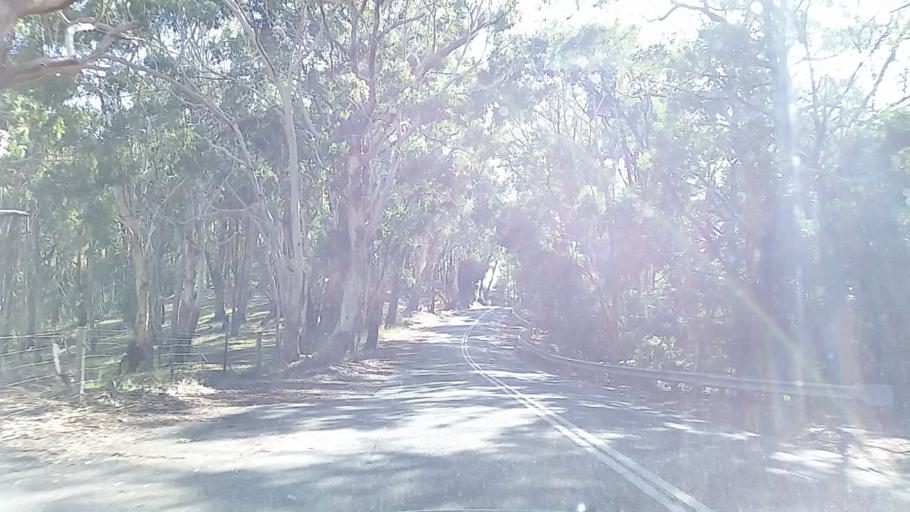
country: AU
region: South Australia
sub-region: Adelaide Hills
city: Crafers
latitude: -34.9642
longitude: 138.7142
